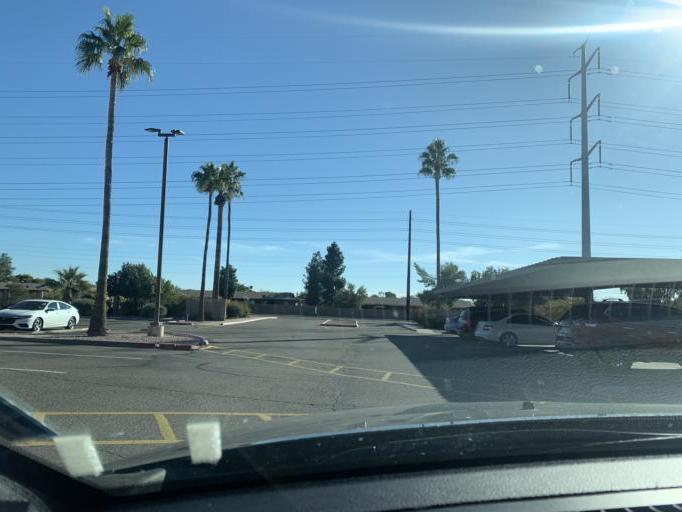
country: US
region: Arizona
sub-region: Maricopa County
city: Gilbert
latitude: 33.4235
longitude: -111.7054
